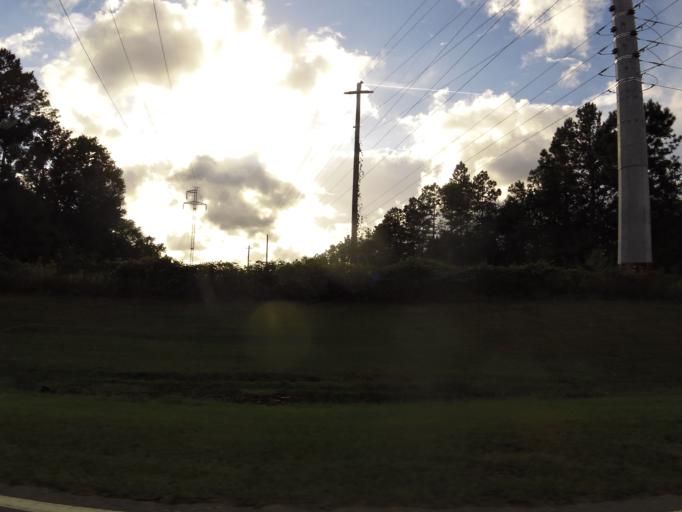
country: US
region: Georgia
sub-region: Liberty County
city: Midway
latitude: 31.7463
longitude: -81.4401
